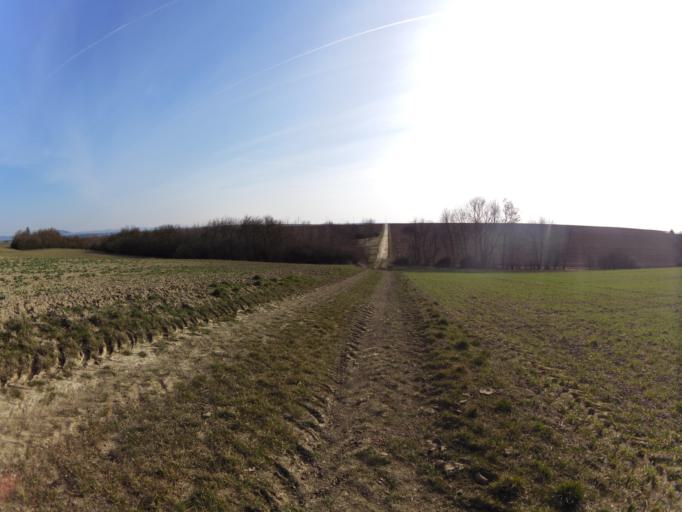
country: DE
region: Bavaria
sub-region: Regierungsbezirk Unterfranken
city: Prosselsheim
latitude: 49.8317
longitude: 10.1341
